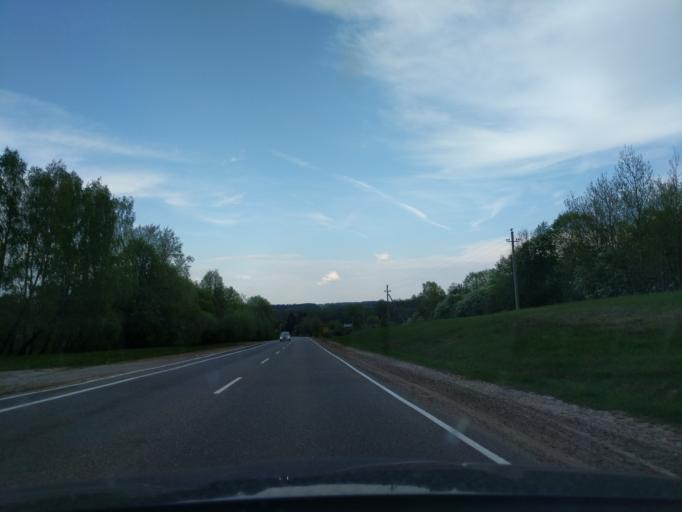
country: BY
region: Grodnenskaya
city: Navahrudak
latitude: 53.6161
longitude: 25.8703
